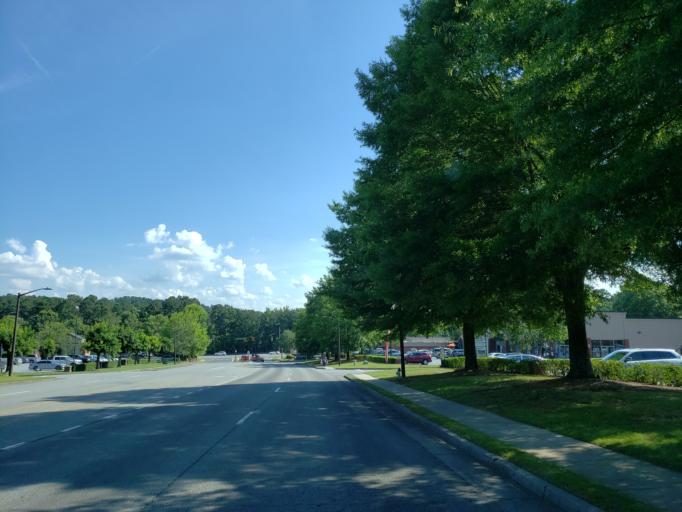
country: US
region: Georgia
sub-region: Cherokee County
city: Woodstock
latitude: 34.1067
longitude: -84.5412
